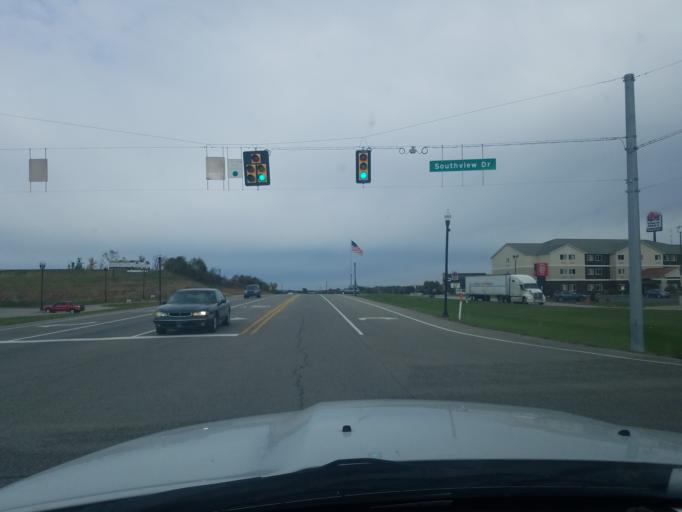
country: US
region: Indiana
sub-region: Dubois County
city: Ferdinand
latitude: 38.2091
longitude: -86.8655
